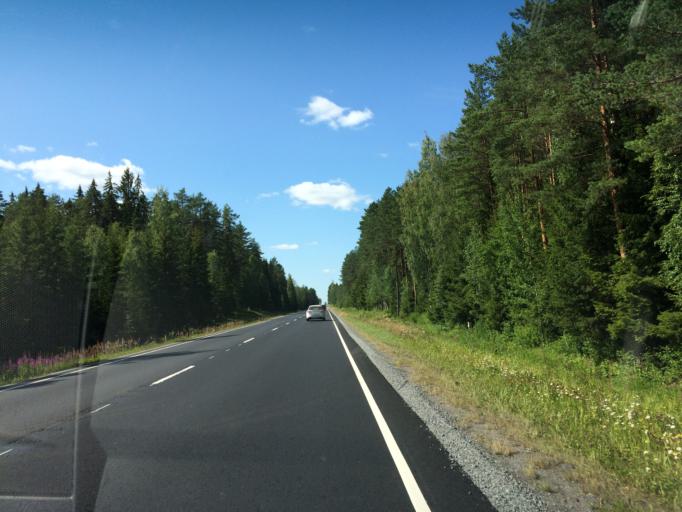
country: FI
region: Pirkanmaa
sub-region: Lounais-Pirkanmaa
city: Kiikoinen
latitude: 61.4736
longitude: 22.4999
